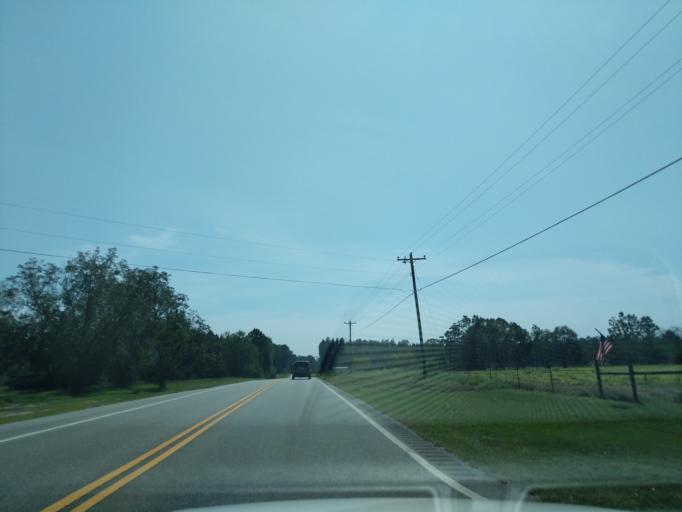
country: US
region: Alabama
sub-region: Covington County
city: Andalusia
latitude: 31.2335
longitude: -86.5278
